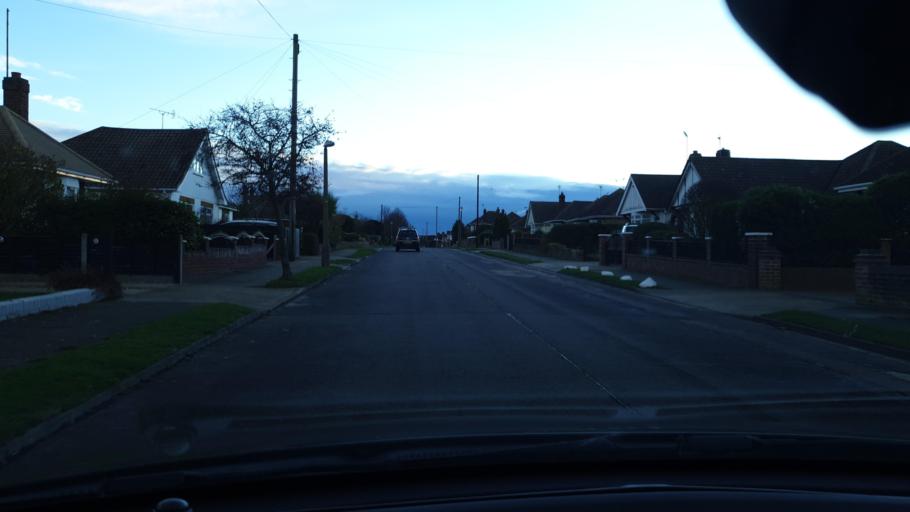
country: GB
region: England
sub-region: Essex
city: Clacton-on-Sea
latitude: 51.7999
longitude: 1.1653
